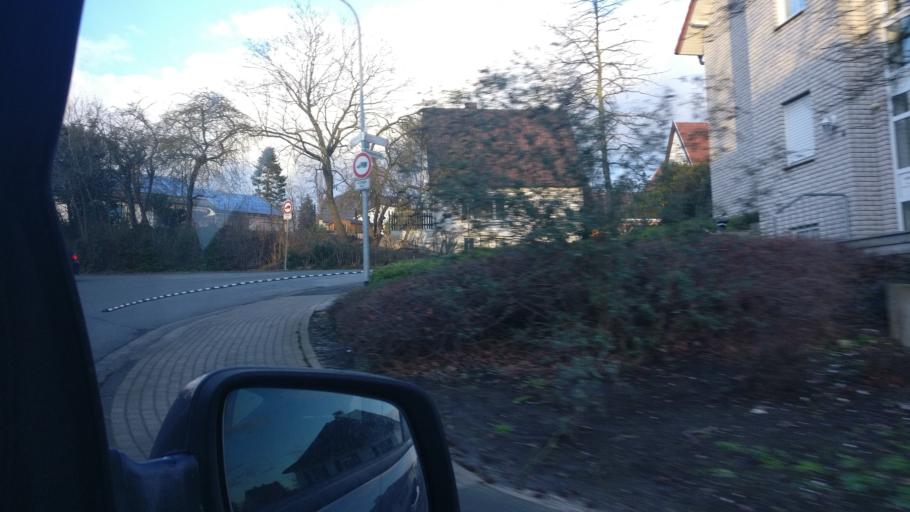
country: DE
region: North Rhine-Westphalia
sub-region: Regierungsbezirk Detmold
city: Lage
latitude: 51.9968
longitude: 8.7950
